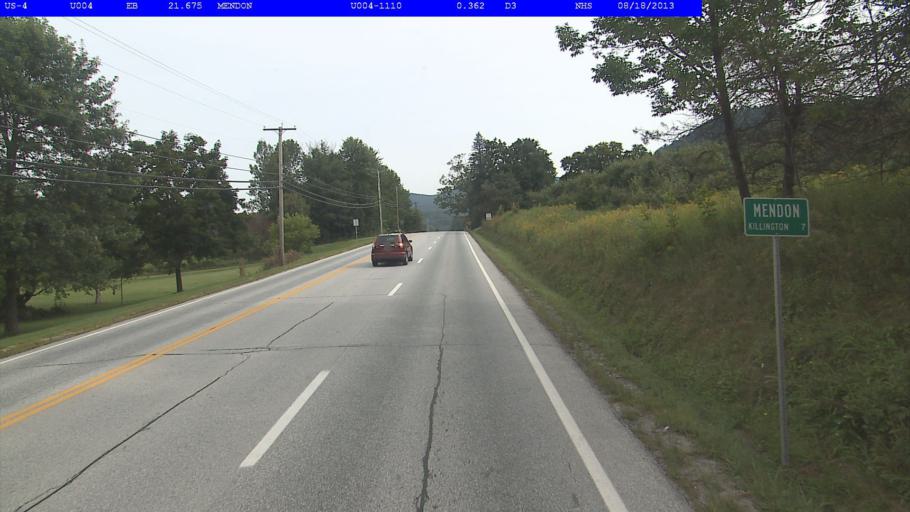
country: US
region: Vermont
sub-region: Rutland County
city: Rutland
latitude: 43.6391
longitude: -72.9333
